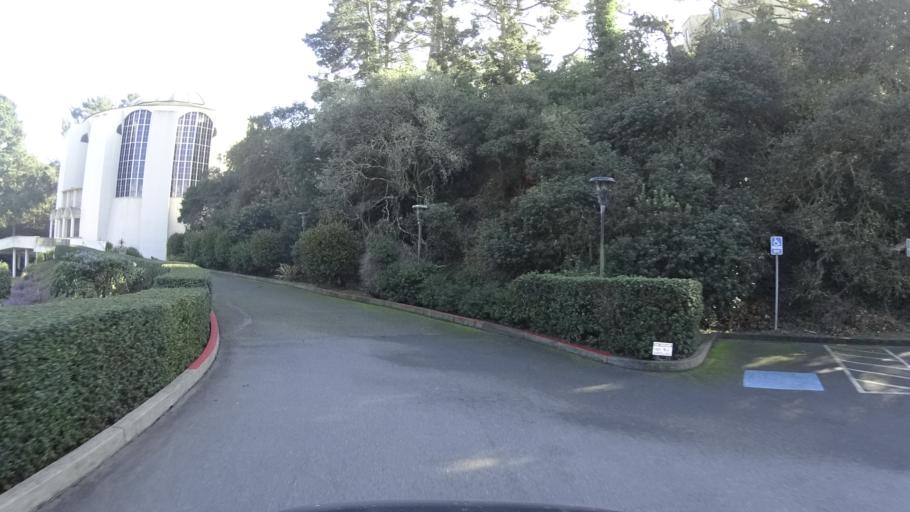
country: US
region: California
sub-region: San Mateo County
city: Daly City
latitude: 37.7138
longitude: -122.4818
